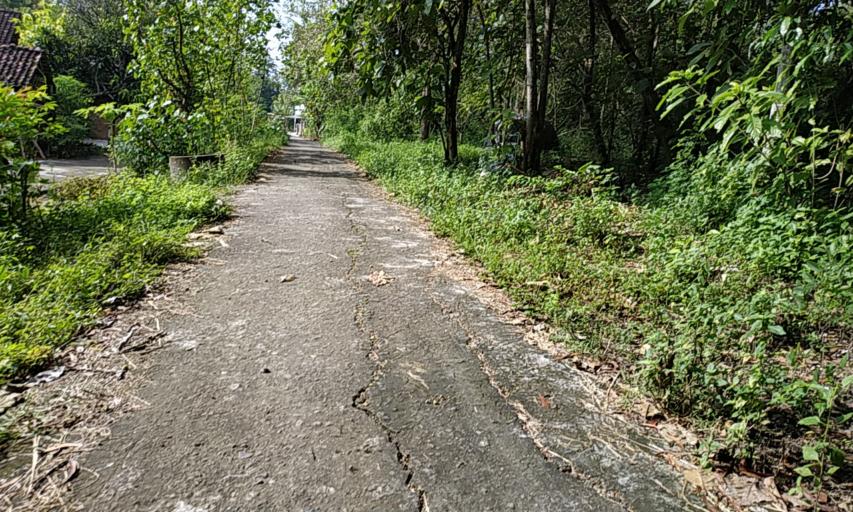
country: ID
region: Central Java
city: Trucuk
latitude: -7.7647
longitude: 110.6818
